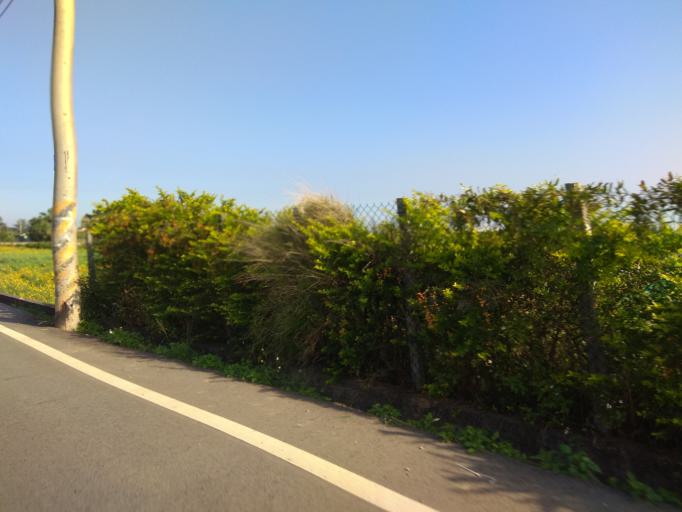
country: TW
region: Taiwan
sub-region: Hsinchu
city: Zhubei
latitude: 24.9805
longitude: 121.0802
